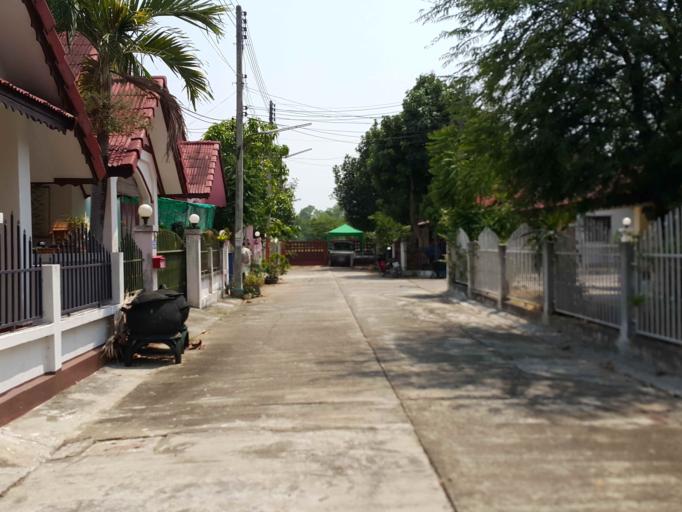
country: TH
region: Chiang Mai
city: San Kamphaeng
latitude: 18.7887
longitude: 99.0943
